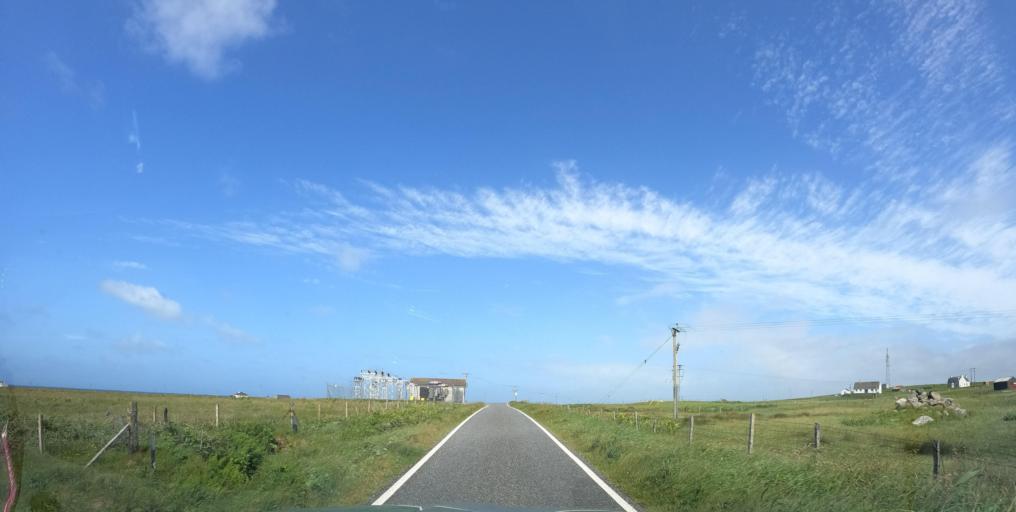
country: GB
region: Scotland
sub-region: Eilean Siar
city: Isle of South Uist
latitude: 57.1060
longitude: -7.3679
